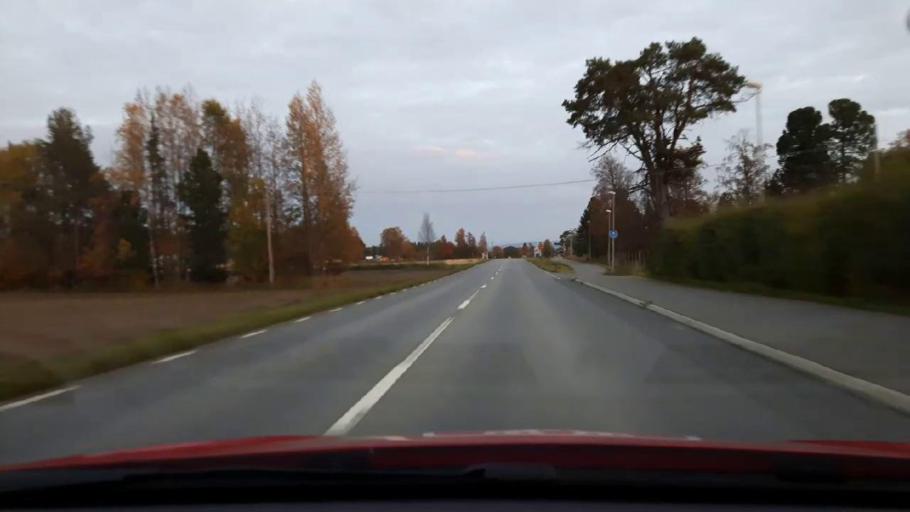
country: SE
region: Jaemtland
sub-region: OEstersunds Kommun
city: Ostersund
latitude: 63.2380
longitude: 14.5753
